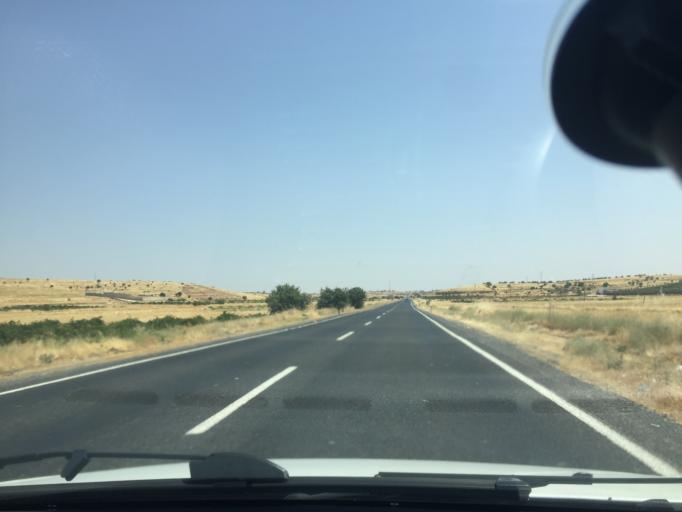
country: TR
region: Mardin
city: Kindirip
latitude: 37.4539
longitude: 41.2524
